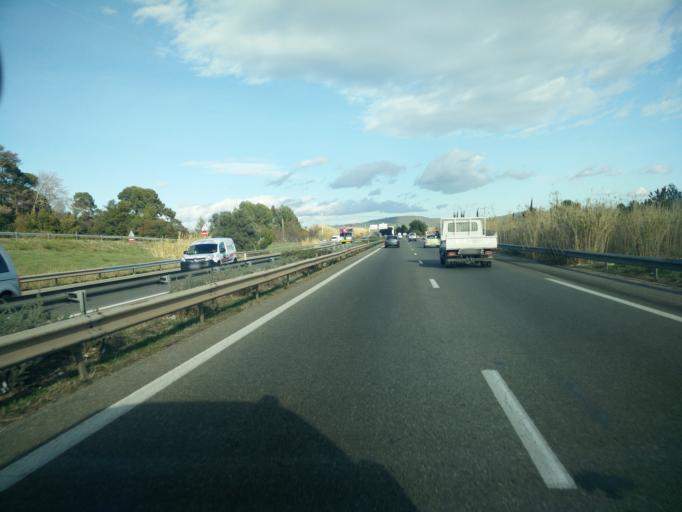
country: FR
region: Provence-Alpes-Cote d'Azur
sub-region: Departement du Var
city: La Farlede
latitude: 43.1587
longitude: 6.0463
